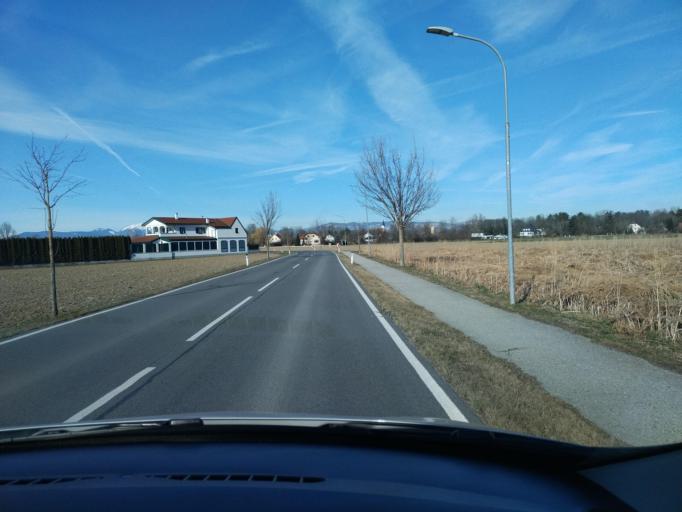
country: AT
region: Lower Austria
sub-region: Politischer Bezirk Wiener Neustadt
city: Lanzenkirchen
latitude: 47.7385
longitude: 16.2484
